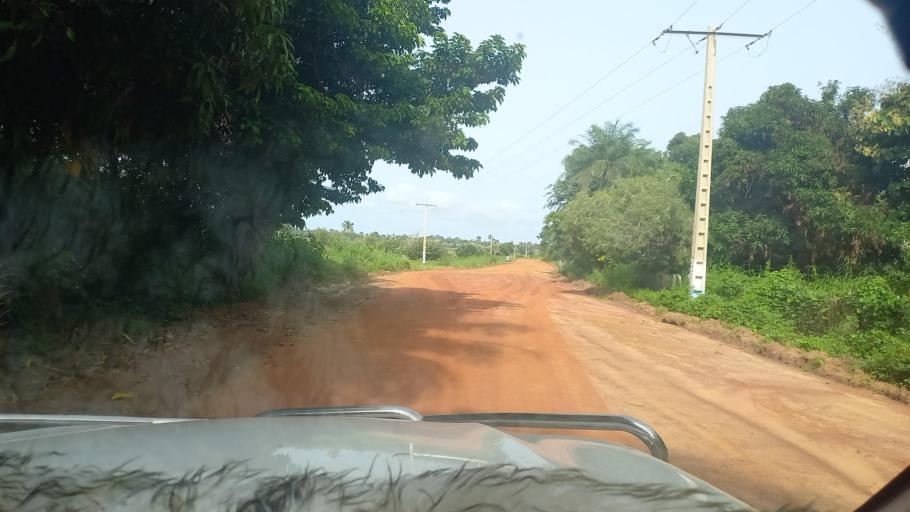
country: SN
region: Ziguinchor
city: Ziguinchor
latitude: 12.6706
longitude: -16.2757
